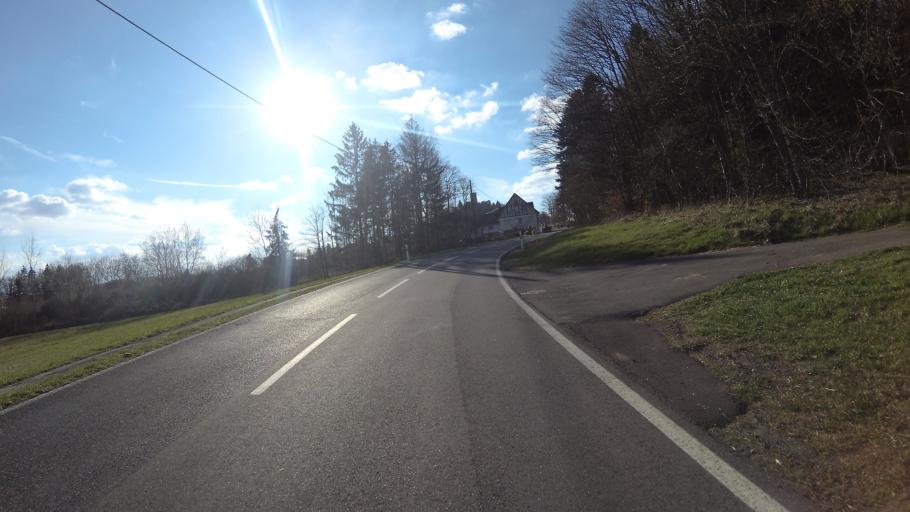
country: DE
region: Rheinland-Pfalz
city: Meuspath
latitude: 50.3462
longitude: 6.9618
